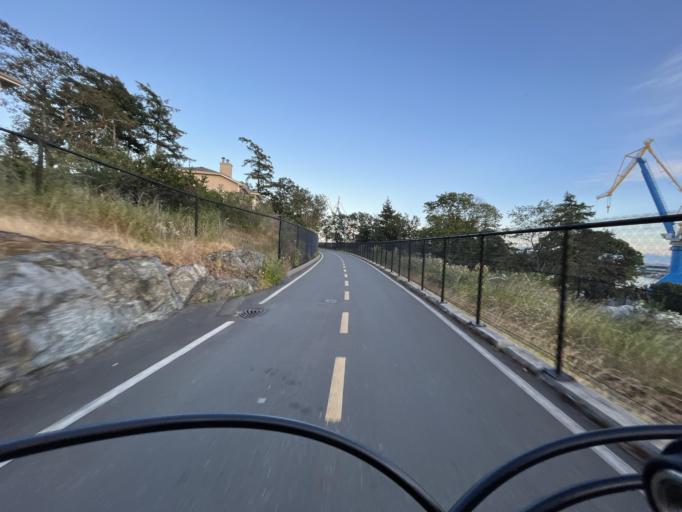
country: CA
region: British Columbia
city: Colwood
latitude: 48.4387
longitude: -123.4283
